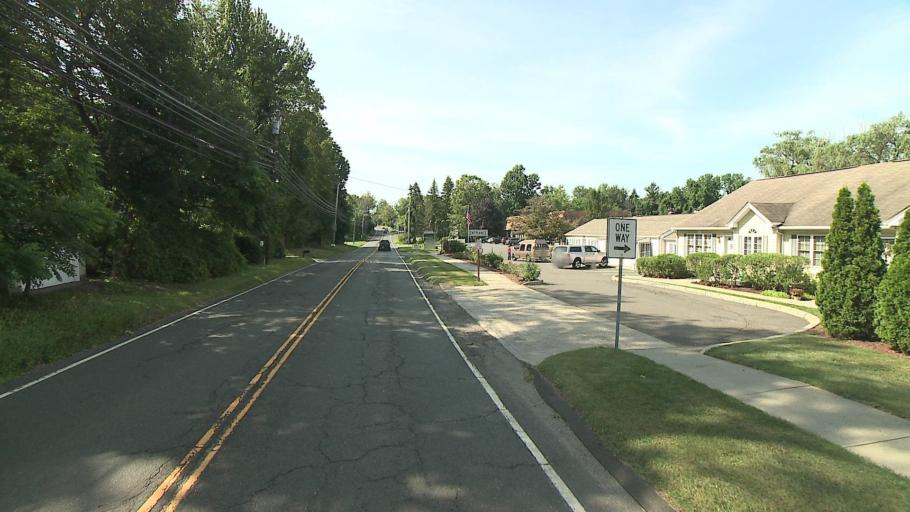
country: US
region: Connecticut
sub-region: Fairfield County
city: Danbury
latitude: 41.4450
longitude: -73.4725
